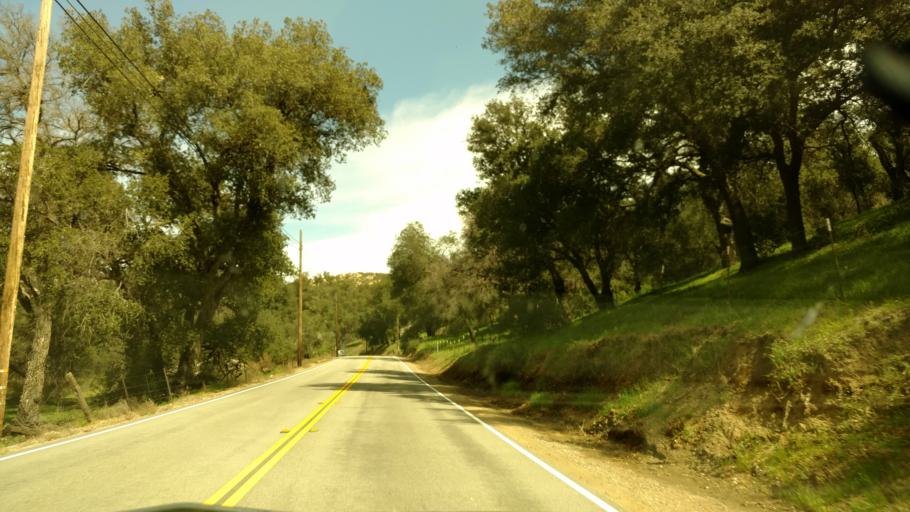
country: US
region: California
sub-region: San Diego County
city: Julian
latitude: 33.0855
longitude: -116.7091
